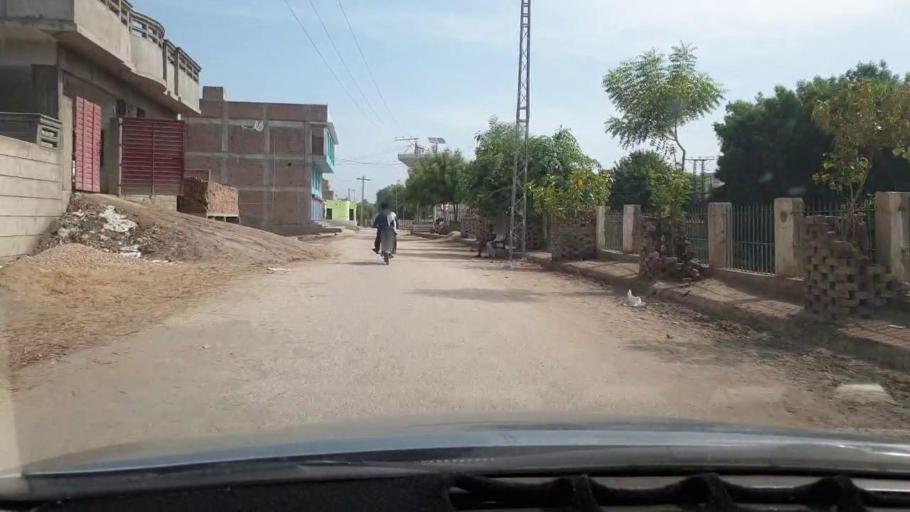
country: PK
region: Sindh
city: Khairpur
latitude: 27.5318
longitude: 68.7529
